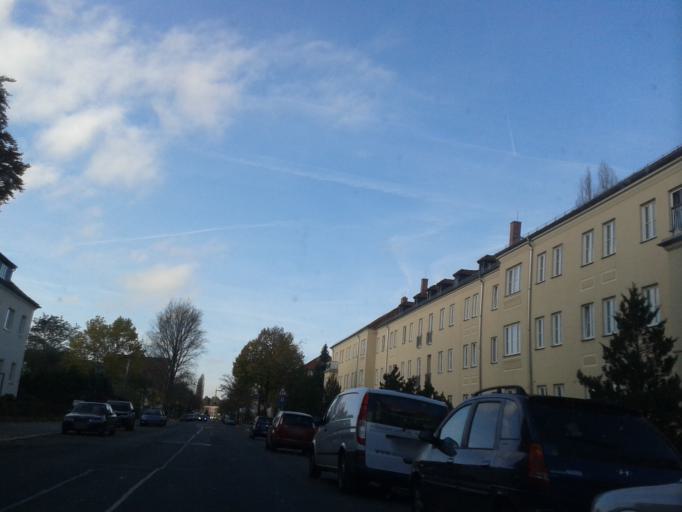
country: DE
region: Saxony
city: Dresden
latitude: 51.0888
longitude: 13.7126
